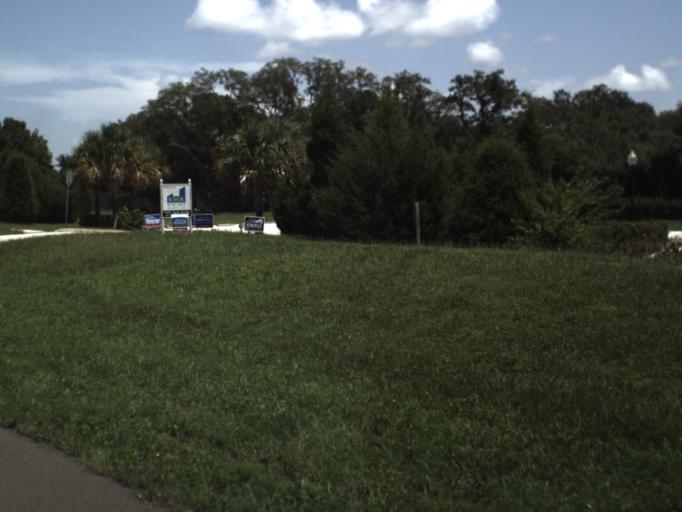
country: US
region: Florida
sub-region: Pinellas County
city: Tarpon Springs
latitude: 28.1135
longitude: -82.7685
